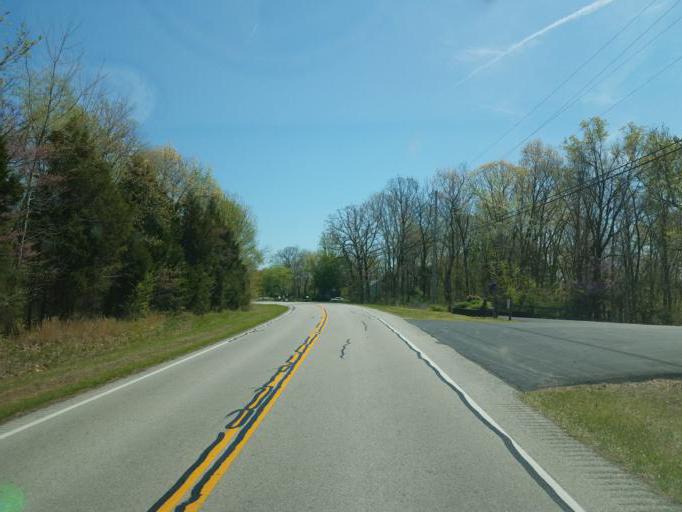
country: US
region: Kentucky
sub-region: Barren County
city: Cave City
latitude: 37.1314
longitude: -86.0286
